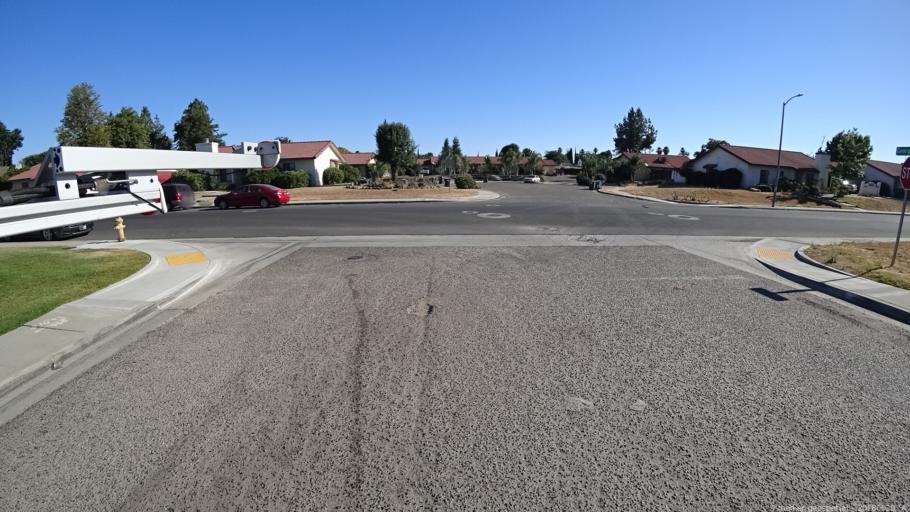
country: US
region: California
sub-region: Madera County
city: Parkwood
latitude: 36.9313
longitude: -120.0541
